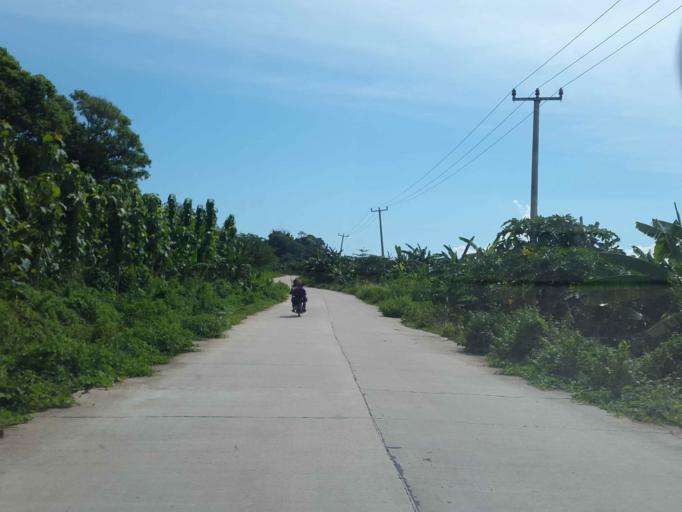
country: ID
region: Banten
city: Babakanbungur
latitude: -6.5228
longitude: 105.6295
